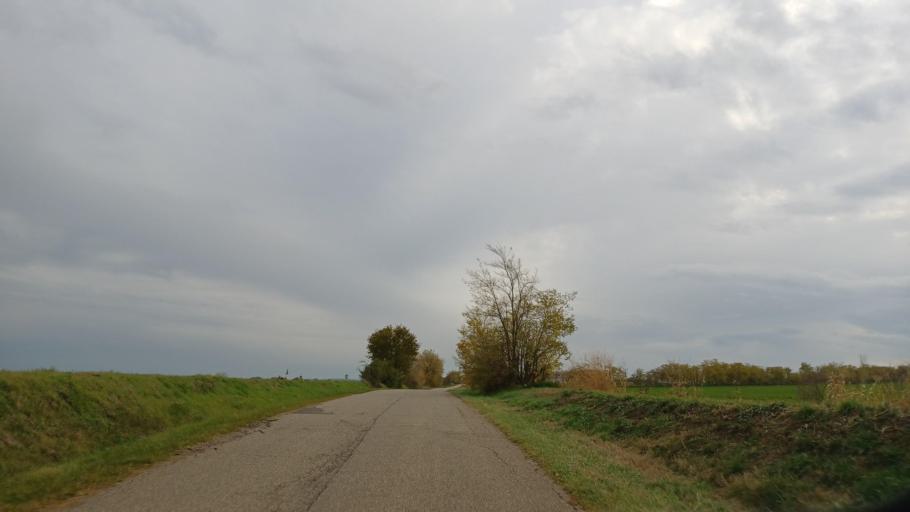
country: HU
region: Tolna
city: Nagydorog
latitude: 46.6404
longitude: 18.6064
